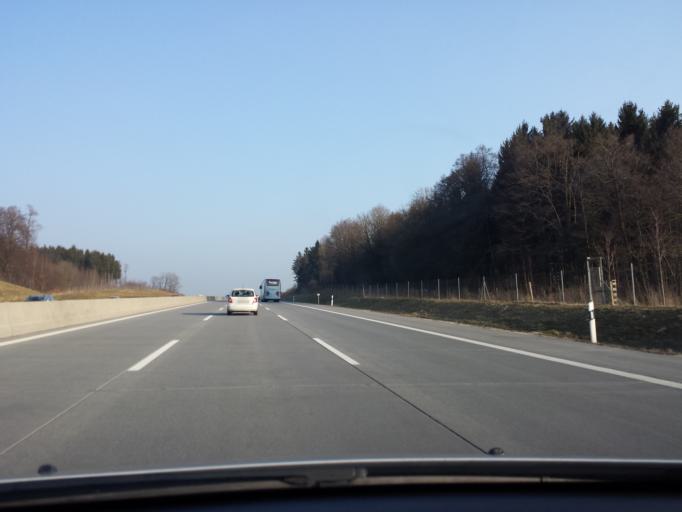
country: DE
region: Bavaria
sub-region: Upper Bavaria
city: Sulzemoos
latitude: 48.2927
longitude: 11.2389
